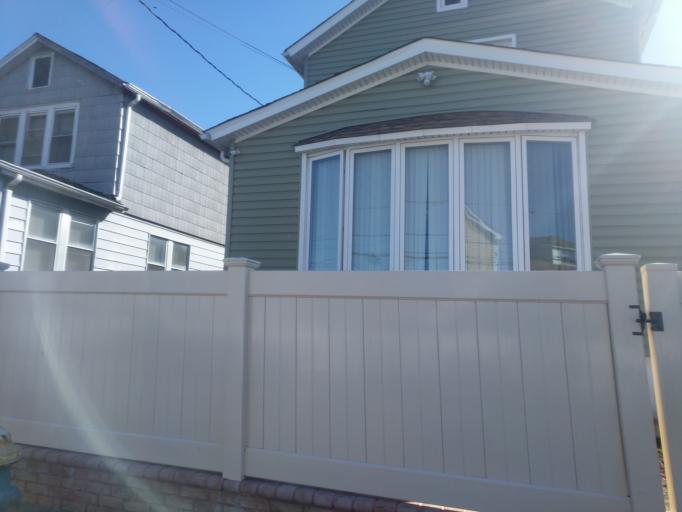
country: US
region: New York
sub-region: Nassau County
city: Inwood
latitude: 40.6128
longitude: -73.7483
